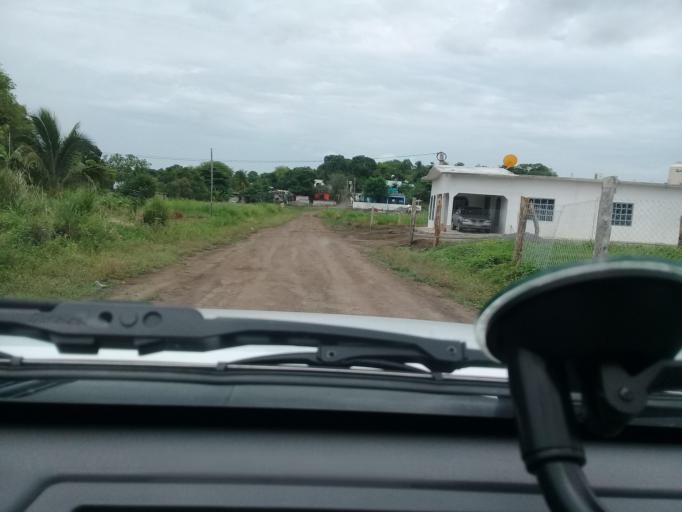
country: MX
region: Veracruz
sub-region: Paso de Ovejas
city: El Hatito
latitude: 19.2765
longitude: -96.3946
